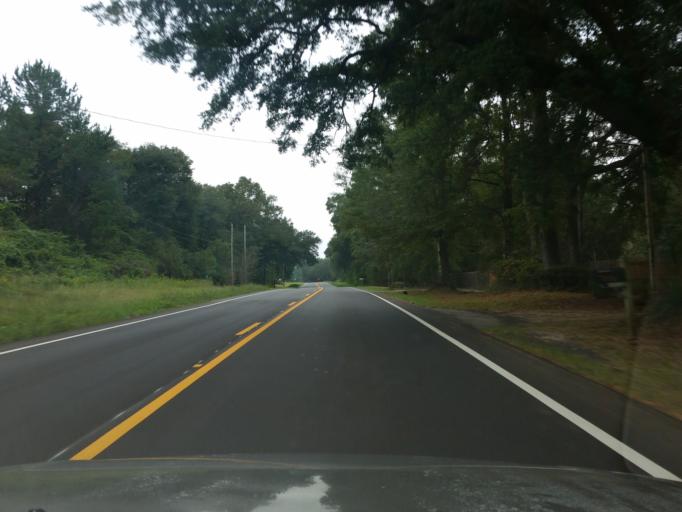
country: US
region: Alabama
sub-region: Baldwin County
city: Spanish Fort
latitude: 30.7718
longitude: -87.8846
